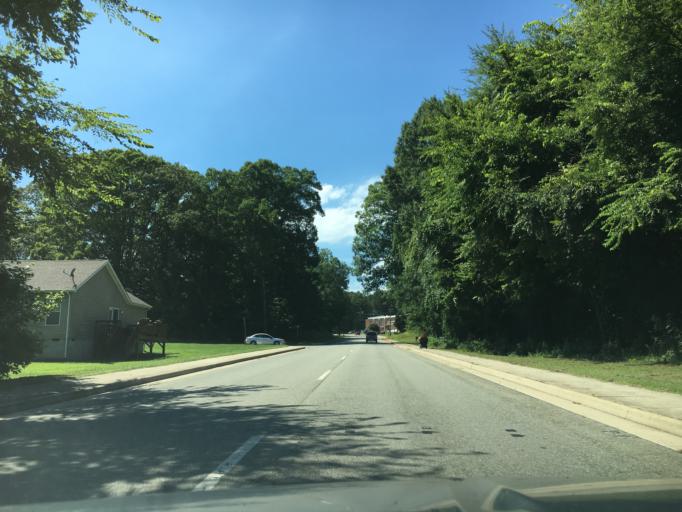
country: US
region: Virginia
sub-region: Halifax County
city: South Boston
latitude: 36.7057
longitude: -78.9060
